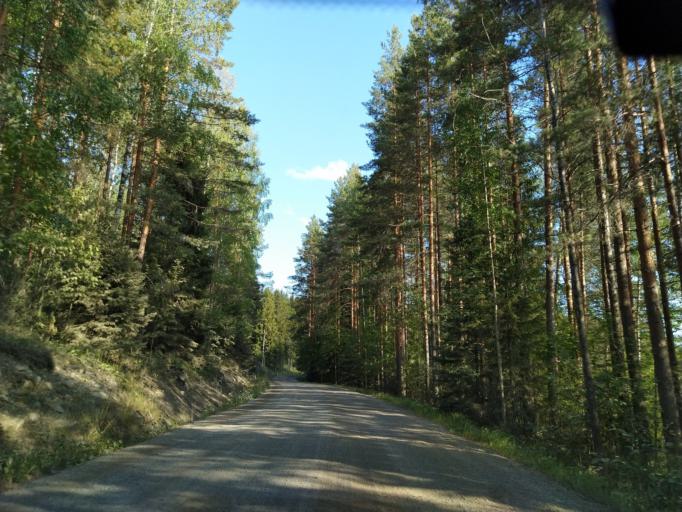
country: FI
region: Central Finland
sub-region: Jaemsae
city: Kuhmoinen
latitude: 61.7047
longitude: 24.9199
